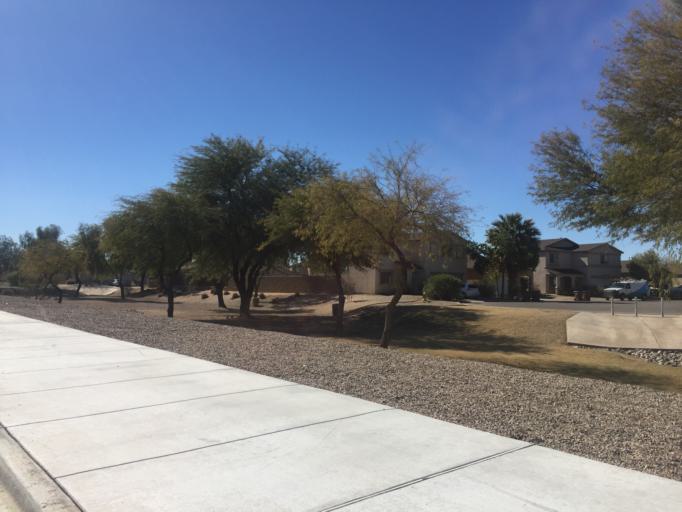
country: US
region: Arizona
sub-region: Pinal County
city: San Tan Valley
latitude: 33.1600
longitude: -111.5450
